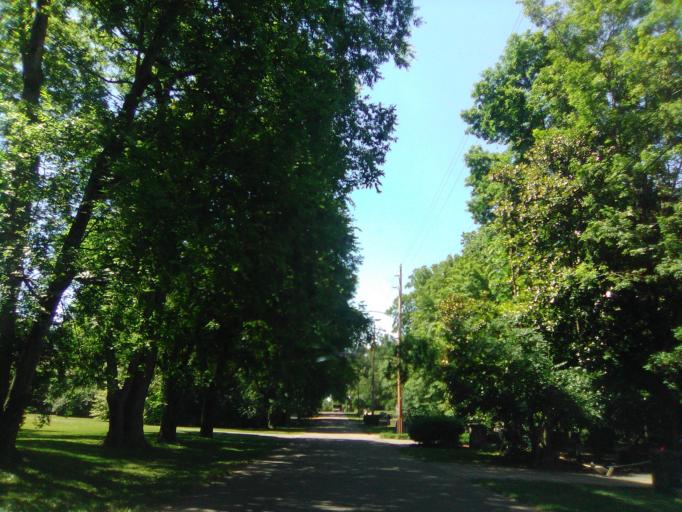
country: US
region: Tennessee
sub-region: Davidson County
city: Belle Meade
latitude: 36.1272
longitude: -86.8398
